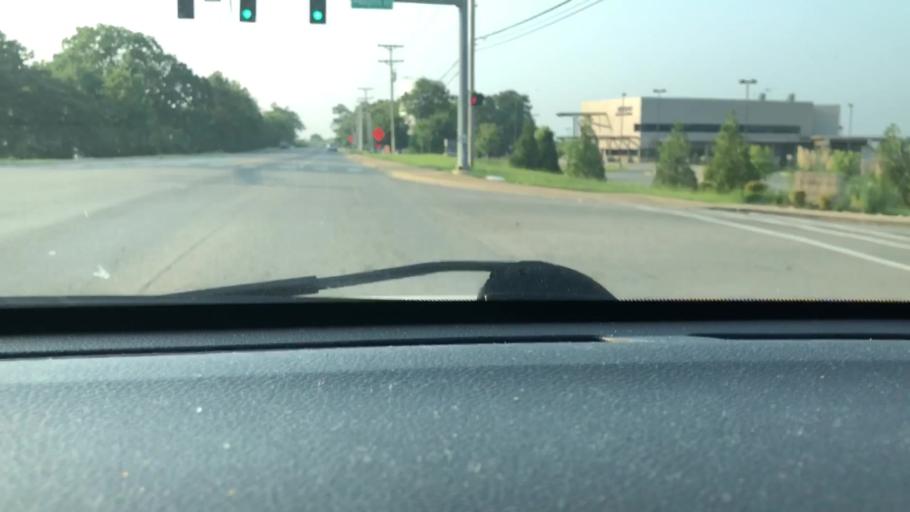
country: US
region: Arkansas
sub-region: Saline County
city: Bryant
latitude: 34.6029
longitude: -92.4908
